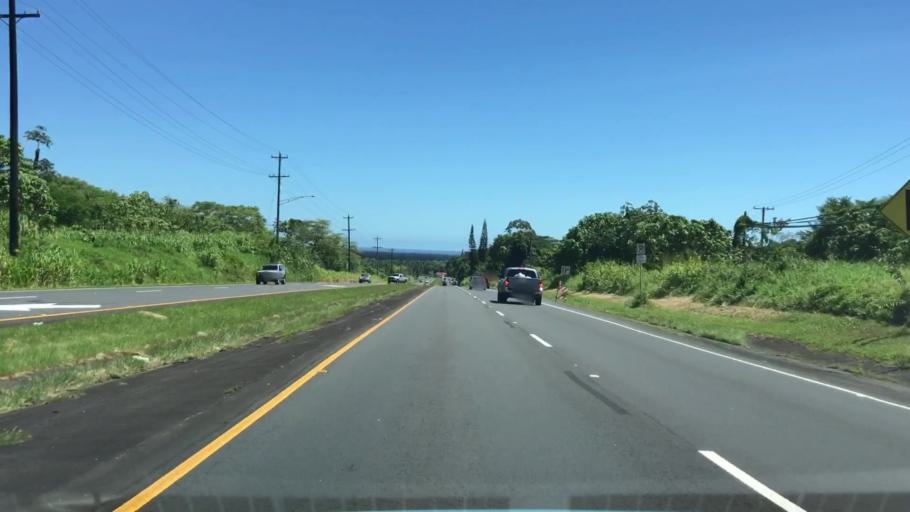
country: US
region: Hawaii
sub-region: Hawaii County
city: Kea'au
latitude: 19.6161
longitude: -155.0455
